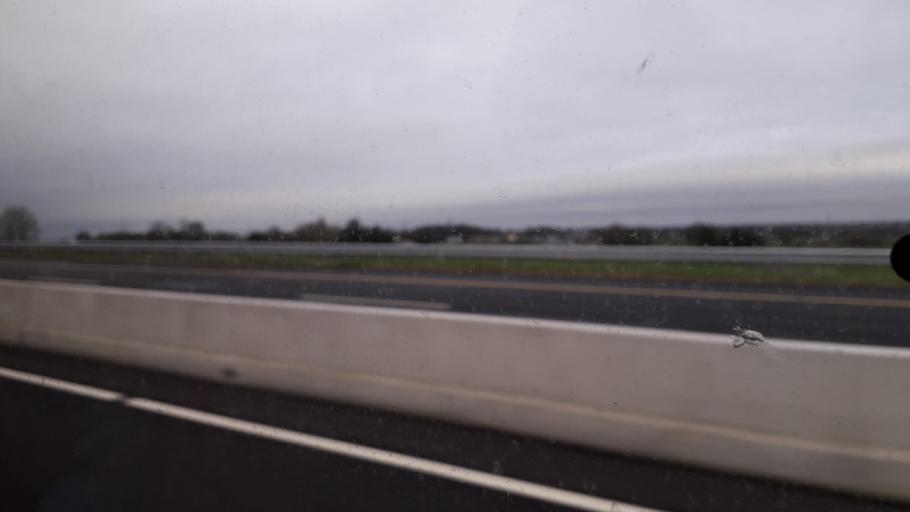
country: IE
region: Connaught
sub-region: County Galway
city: Athenry
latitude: 53.2794
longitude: -8.8017
